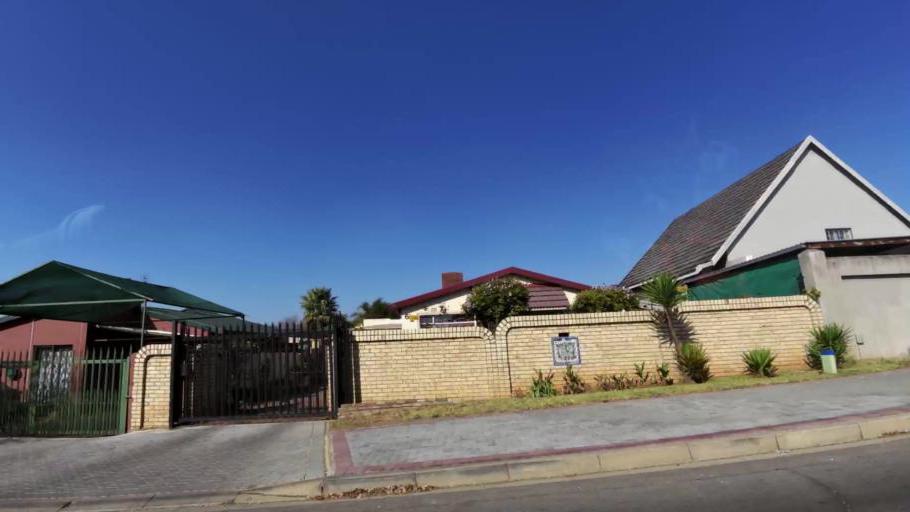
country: ZA
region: Gauteng
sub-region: City of Johannesburg Metropolitan Municipality
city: Johannesburg
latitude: -26.1745
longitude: 27.9846
